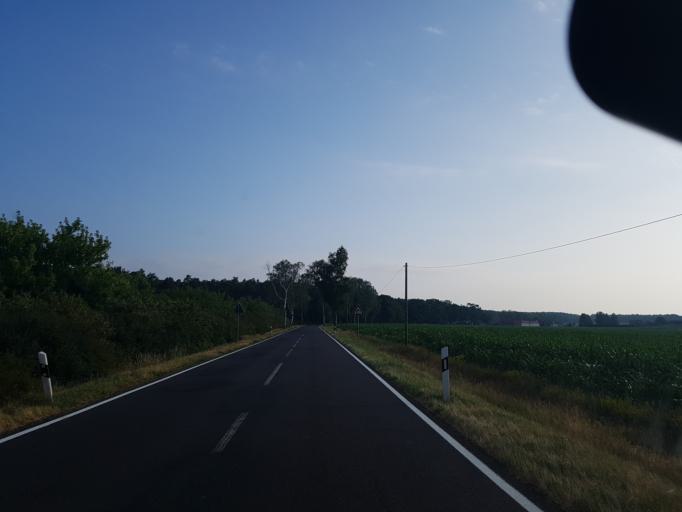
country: DE
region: Brandenburg
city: Schlieben
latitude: 51.7540
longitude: 13.3478
